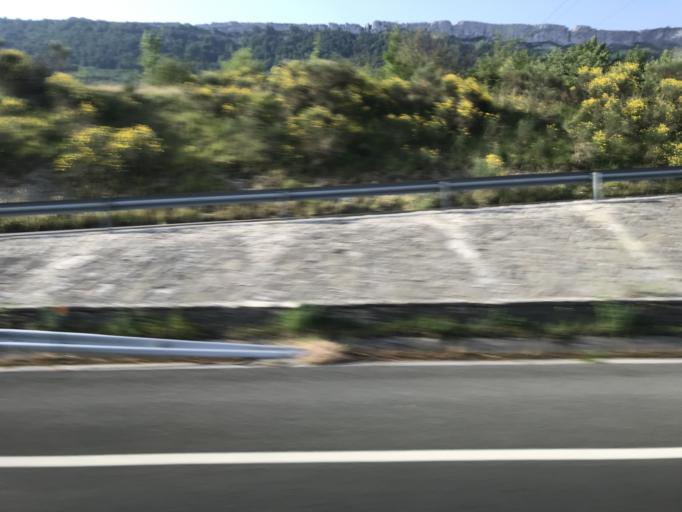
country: ES
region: Navarre
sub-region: Provincia de Navarra
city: Ziordia
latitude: 42.8660
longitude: -2.2349
